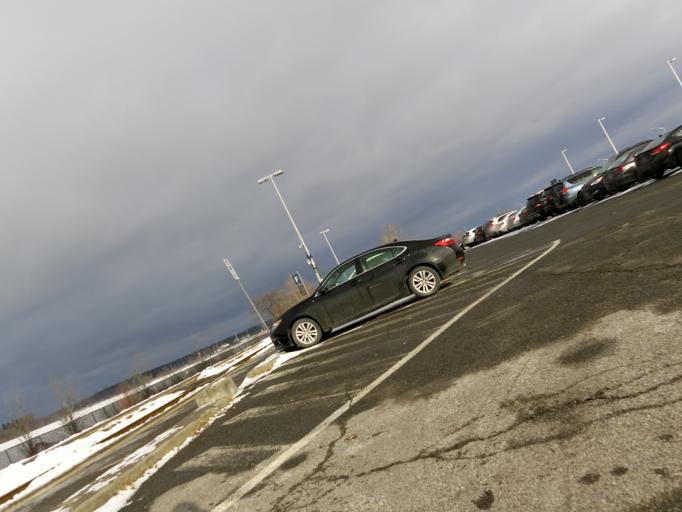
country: CA
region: Ontario
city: Bells Corners
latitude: 45.2997
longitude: -75.7364
